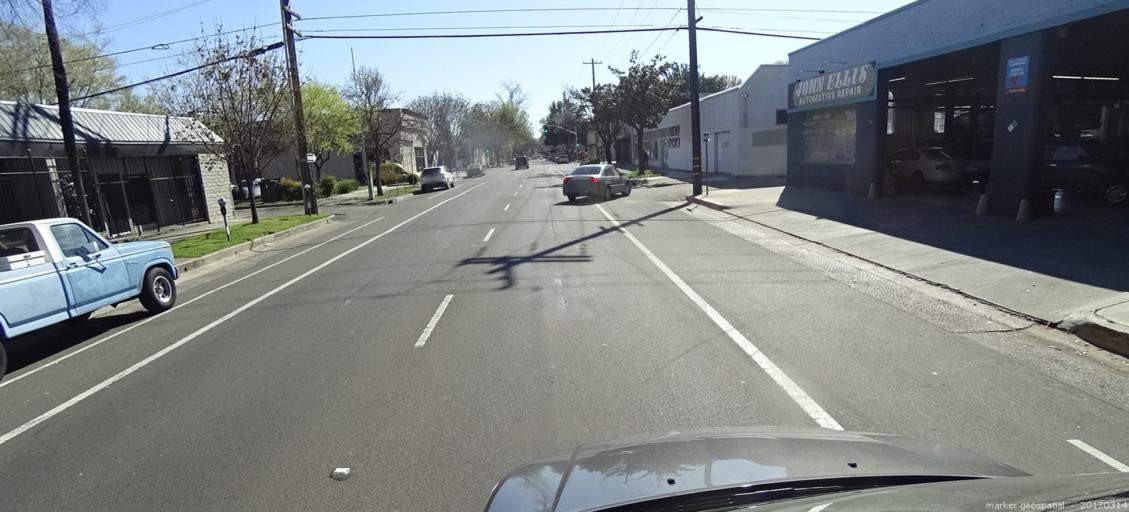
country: US
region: California
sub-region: Sacramento County
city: Sacramento
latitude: 38.5779
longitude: -121.4809
